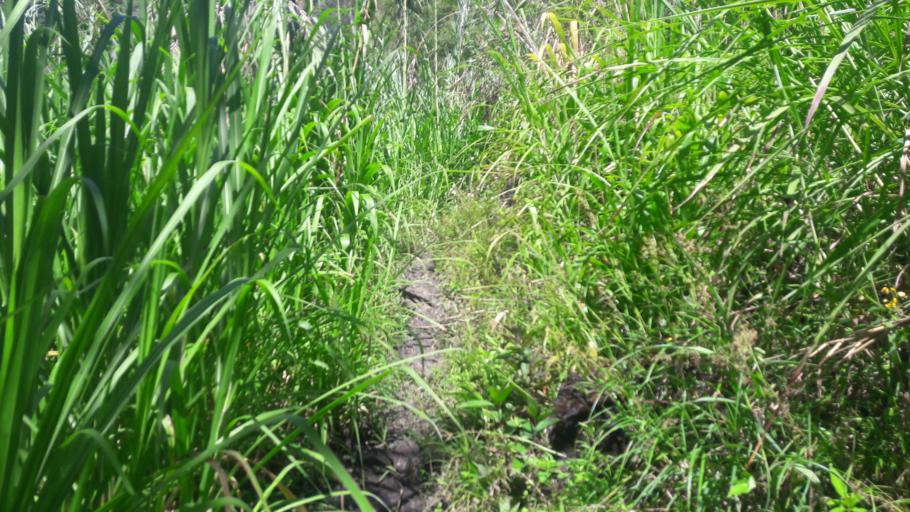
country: CO
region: Cundinamarca
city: Tenza
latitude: 5.0867
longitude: -73.4084
